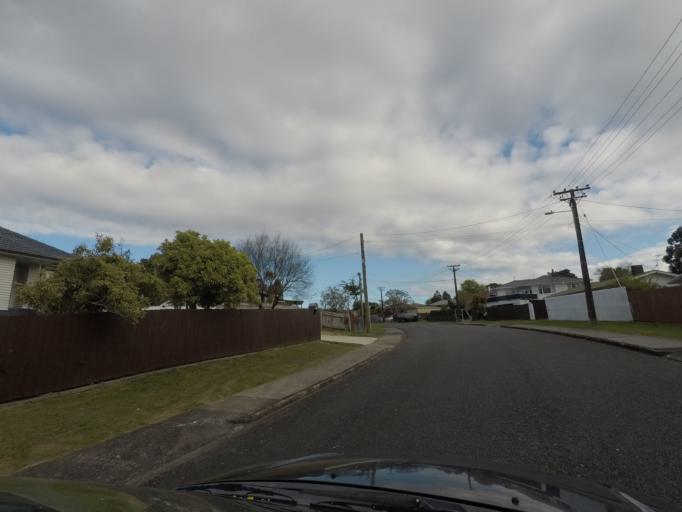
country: NZ
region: Auckland
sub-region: Auckland
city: Rosebank
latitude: -36.8851
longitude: 174.6548
